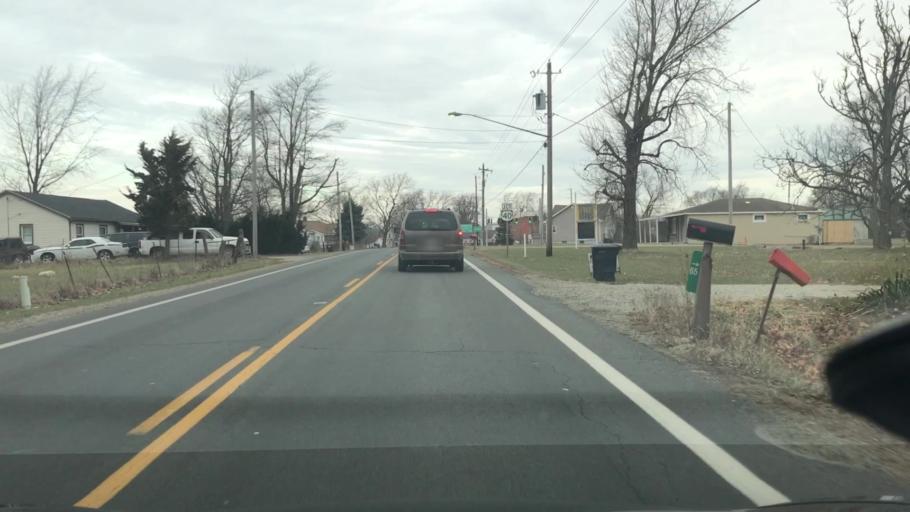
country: US
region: Ohio
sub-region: Madison County
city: Choctaw Lake
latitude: 39.9312
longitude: -83.4910
